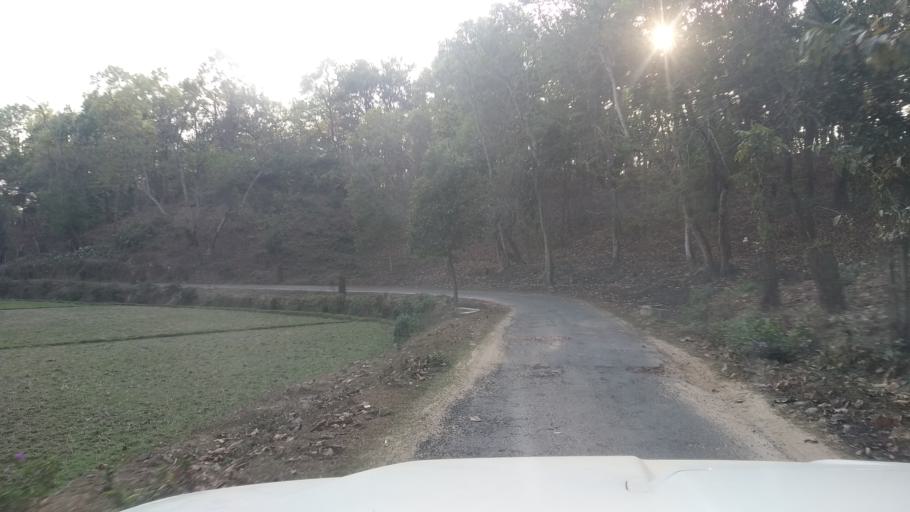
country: IN
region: Tripura
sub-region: West Tripura
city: Sonamura
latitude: 23.3414
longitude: 91.3193
